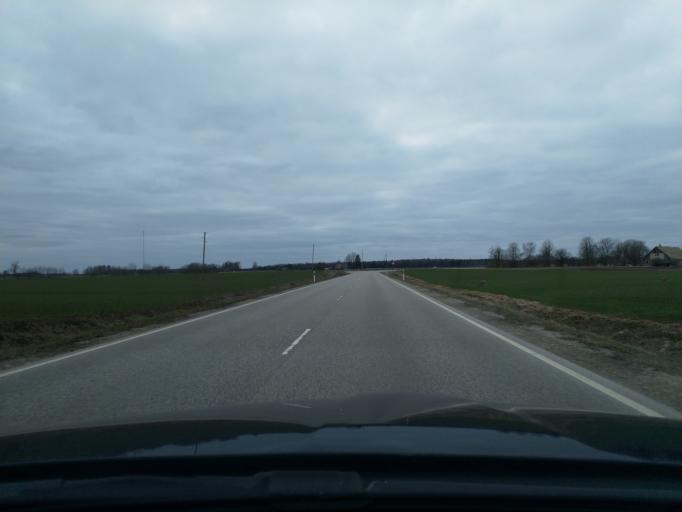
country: LV
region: Talsu Rajons
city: Sabile
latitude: 56.9370
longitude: 22.5014
